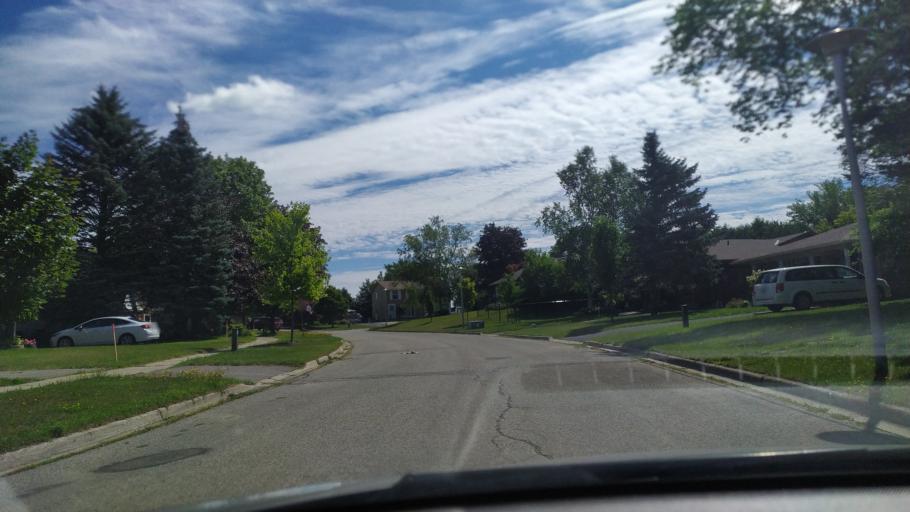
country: CA
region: Ontario
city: Stratford
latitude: 43.3742
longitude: -80.9446
